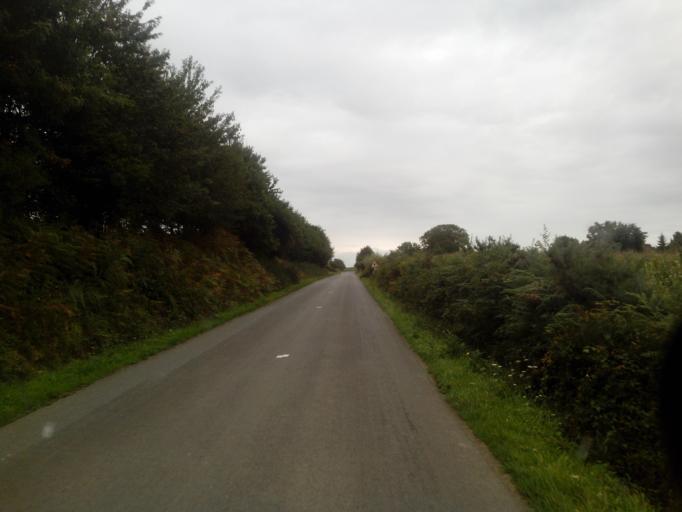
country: FR
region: Brittany
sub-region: Departement d'Ille-et-Vilaine
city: Chevaigne
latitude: 48.2475
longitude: -1.6256
